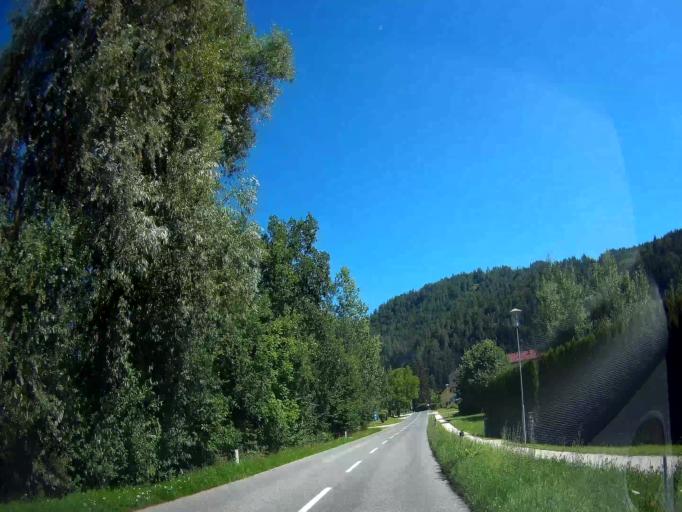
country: AT
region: Carinthia
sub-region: Politischer Bezirk Klagenfurt Land
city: Ebenthal
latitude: 46.6058
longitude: 14.4059
